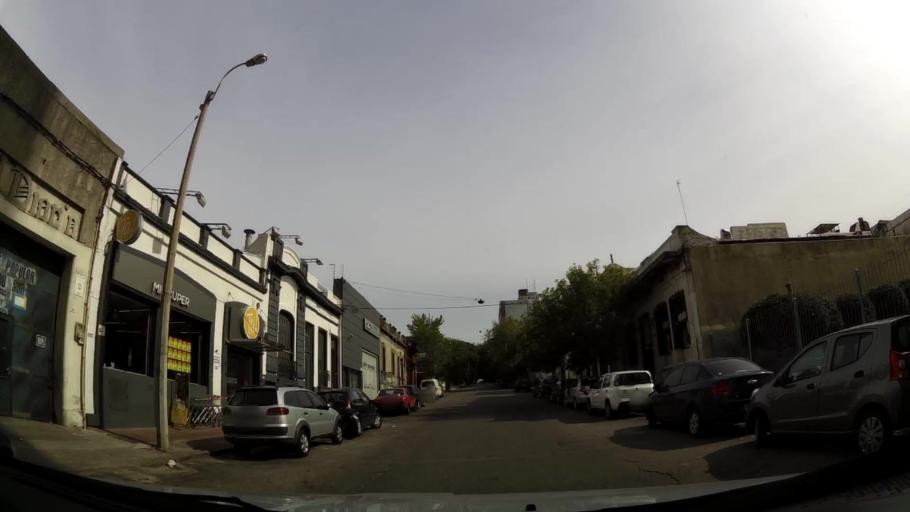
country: UY
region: Montevideo
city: Montevideo
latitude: -34.9120
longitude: -56.1918
